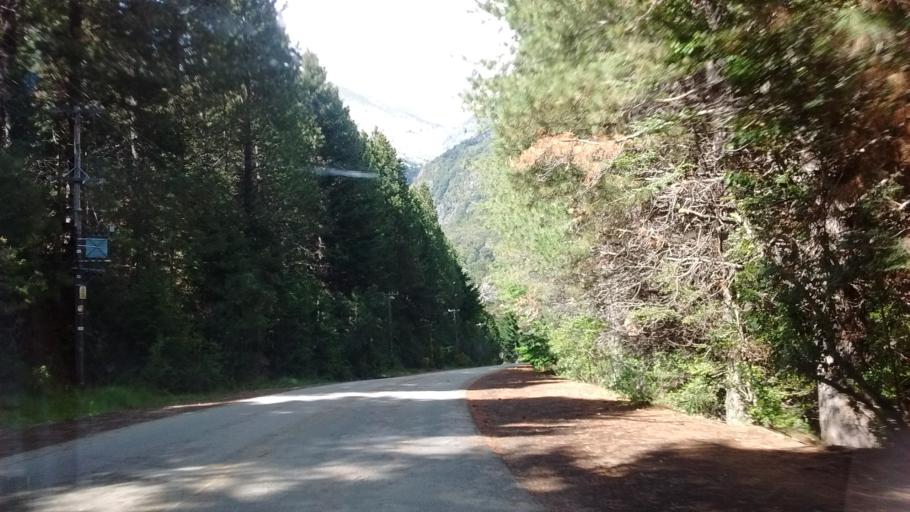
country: AR
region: Rio Negro
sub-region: Departamento de Bariloche
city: San Carlos de Bariloche
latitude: -41.0748
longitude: -71.5450
